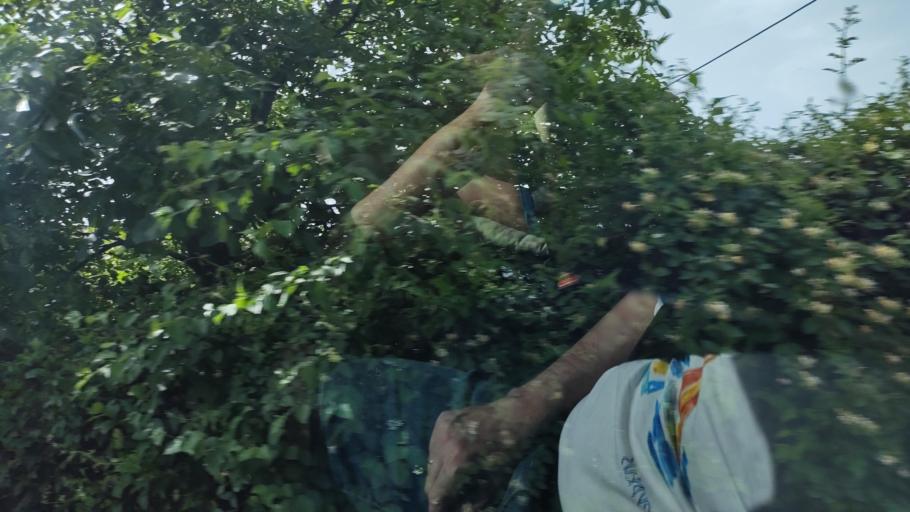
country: RO
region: Mehedinti
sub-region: Comuna Eselnita
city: Eselnita
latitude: 44.6820
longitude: 22.3501
